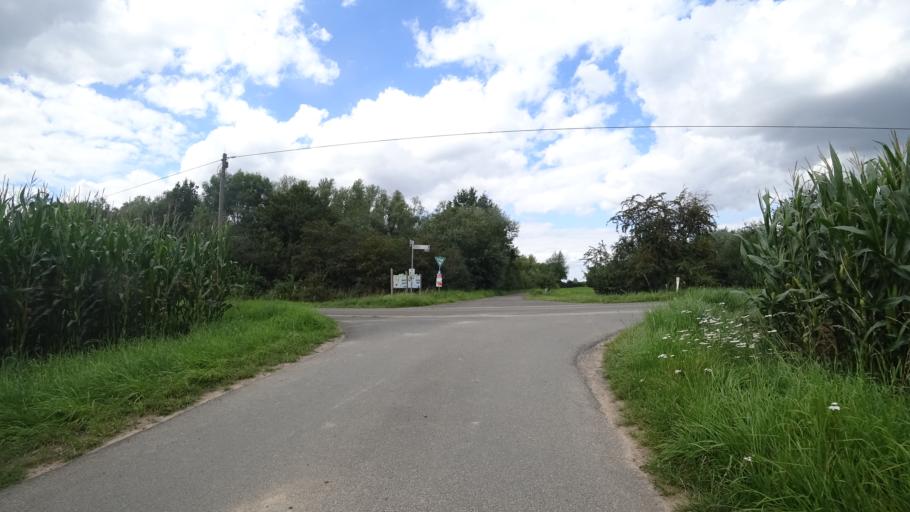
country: DE
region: North Rhine-Westphalia
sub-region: Regierungsbezirk Detmold
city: Petershagen
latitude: 52.4067
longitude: 8.9899
